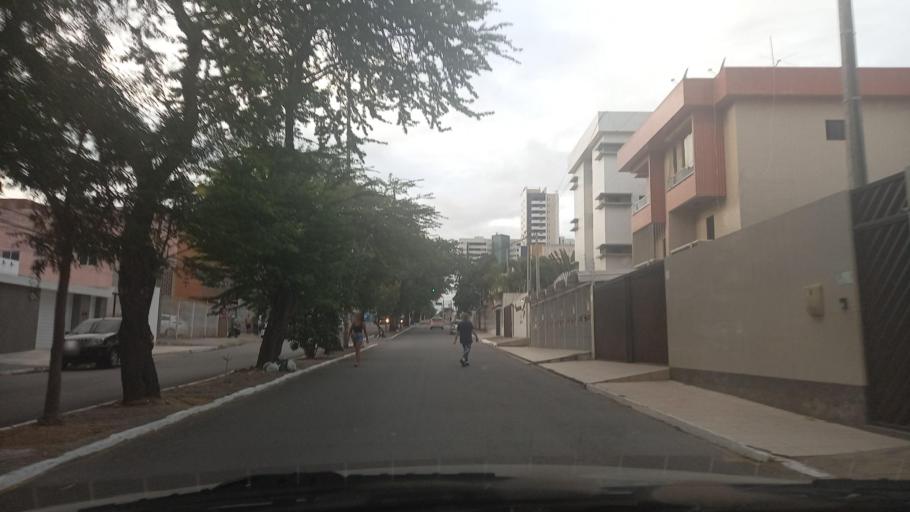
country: BR
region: Pernambuco
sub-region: Caruaru
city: Caruaru
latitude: -8.2722
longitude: -35.9639
